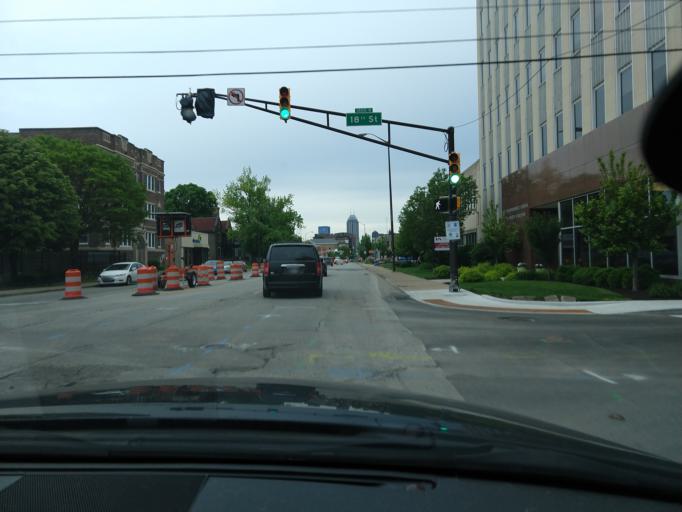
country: US
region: Indiana
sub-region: Marion County
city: Indianapolis
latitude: 39.7908
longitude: -86.1574
